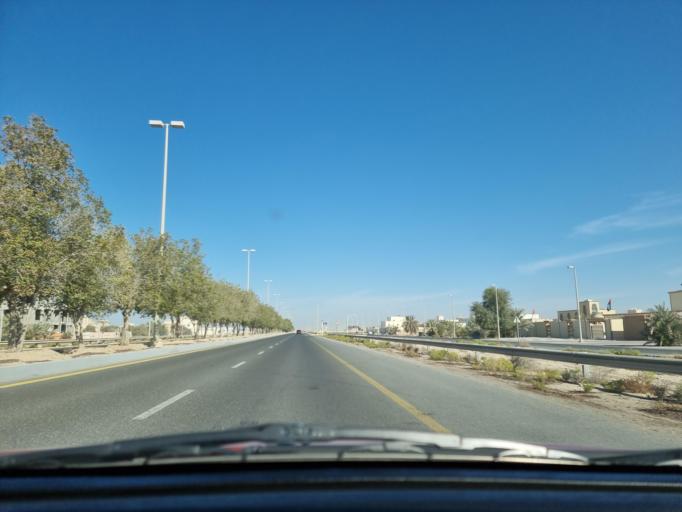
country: AE
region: Abu Dhabi
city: Abu Dhabi
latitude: 24.3926
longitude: 54.6945
